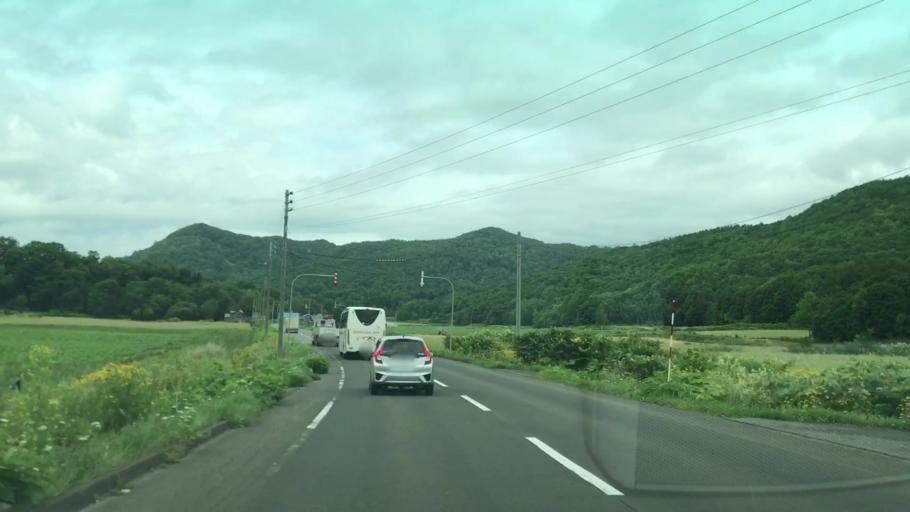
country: JP
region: Hokkaido
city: Niseko Town
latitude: 42.9467
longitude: 140.8380
